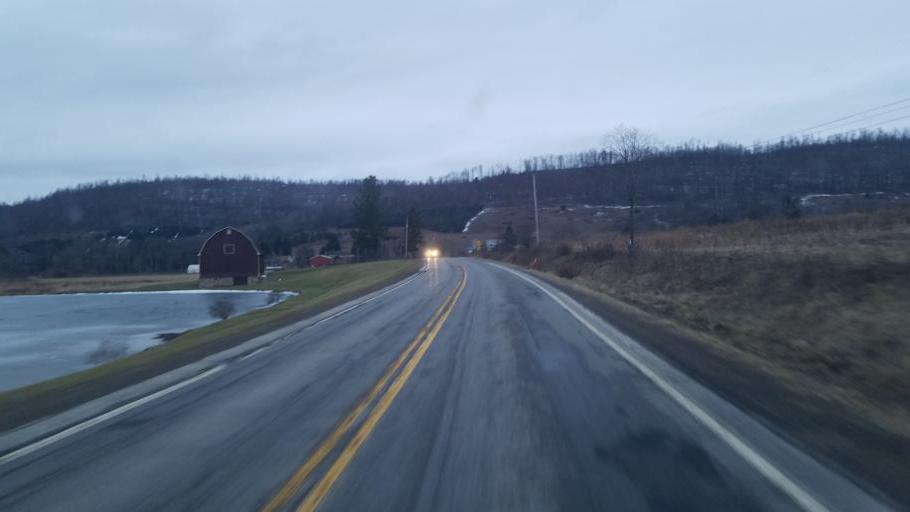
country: US
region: Pennsylvania
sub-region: Potter County
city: Coudersport
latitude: 41.8356
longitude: -77.9367
